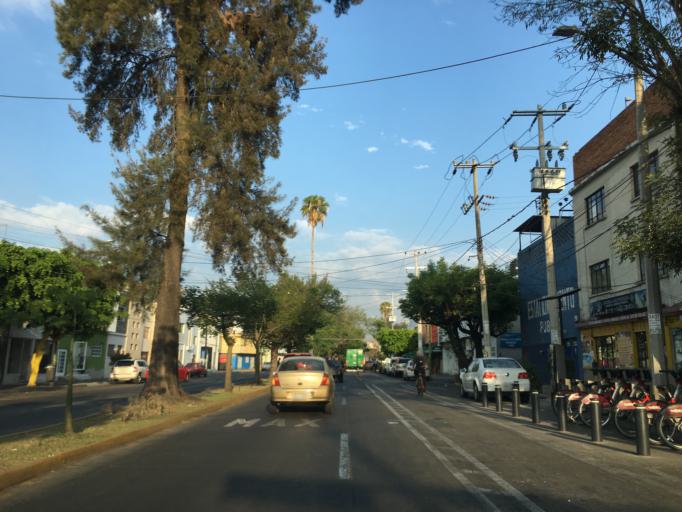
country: MX
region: Jalisco
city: Guadalajara
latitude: 20.6703
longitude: -103.3596
